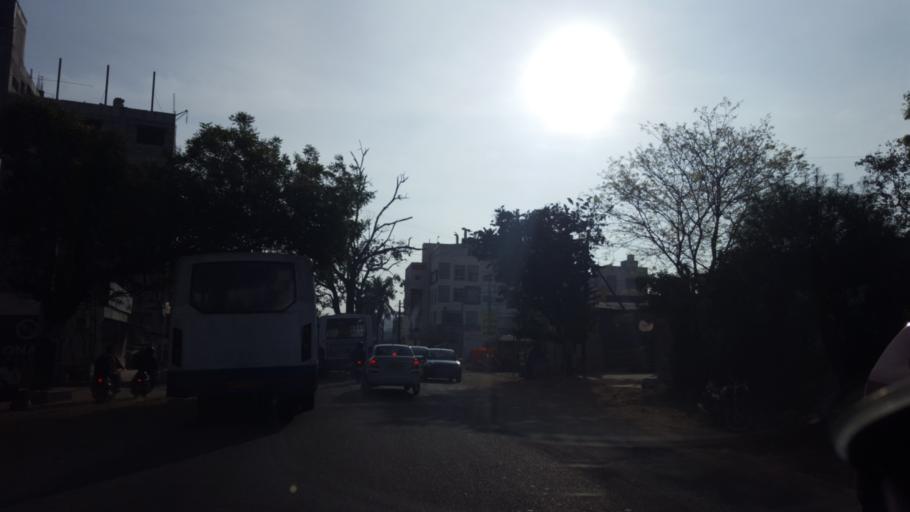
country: IN
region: Karnataka
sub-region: Bangalore Urban
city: Bangalore
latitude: 12.9039
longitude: 77.5079
